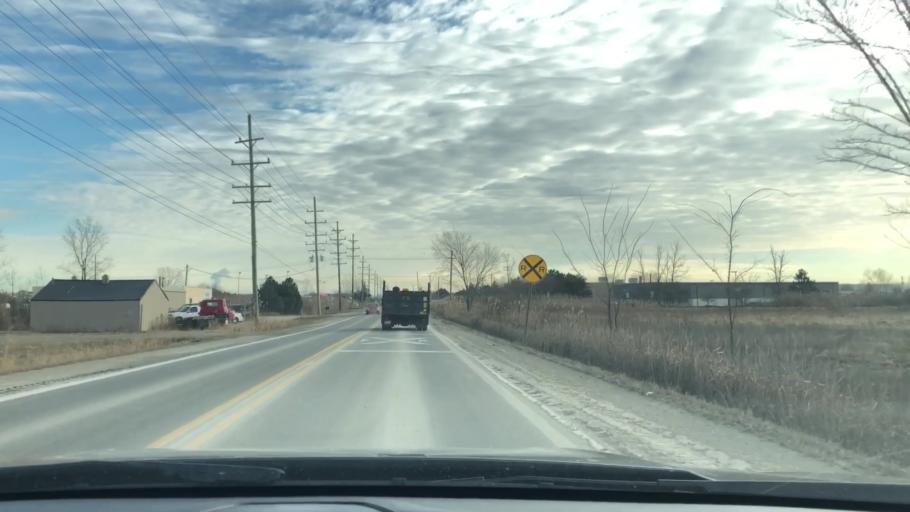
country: US
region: Michigan
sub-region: Macomb County
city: New Haven
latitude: 42.7190
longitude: -82.8104
